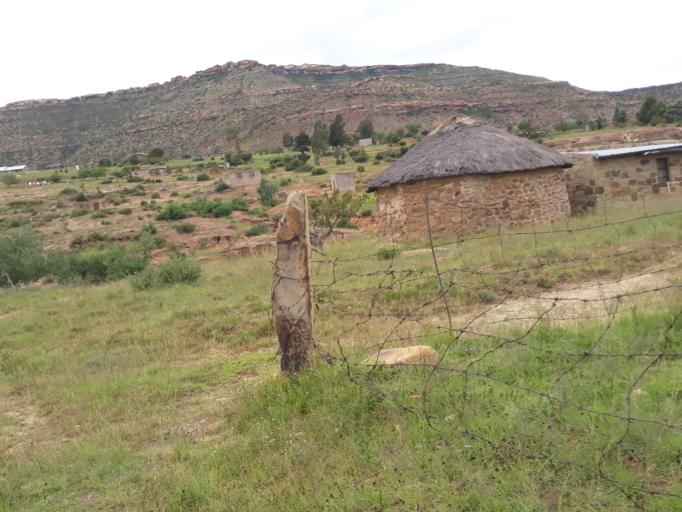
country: LS
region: Quthing
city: Quthing
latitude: -30.3363
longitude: 27.5296
